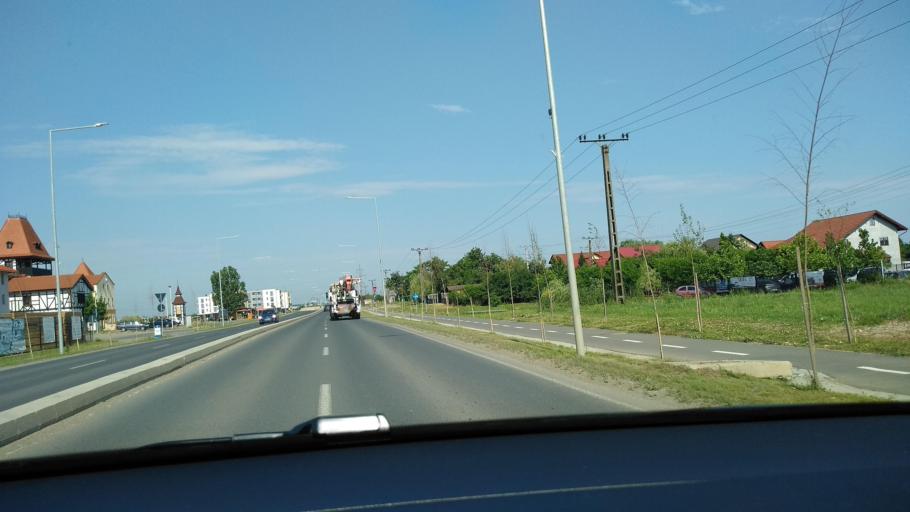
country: RO
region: Timis
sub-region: Comuna Mosnita Noua
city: Mosnita Noua
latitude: 45.7234
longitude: 21.2977
